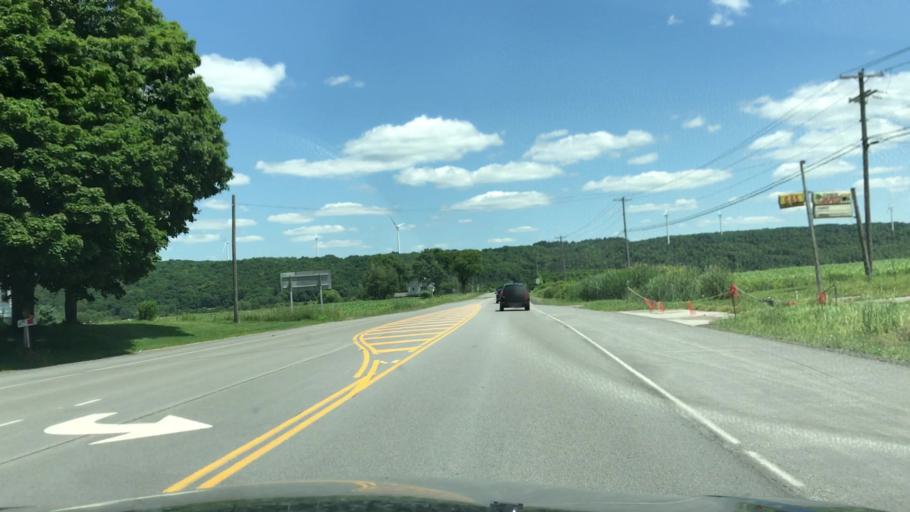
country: US
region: New York
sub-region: Wyoming County
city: Attica
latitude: 42.7703
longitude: -78.3882
